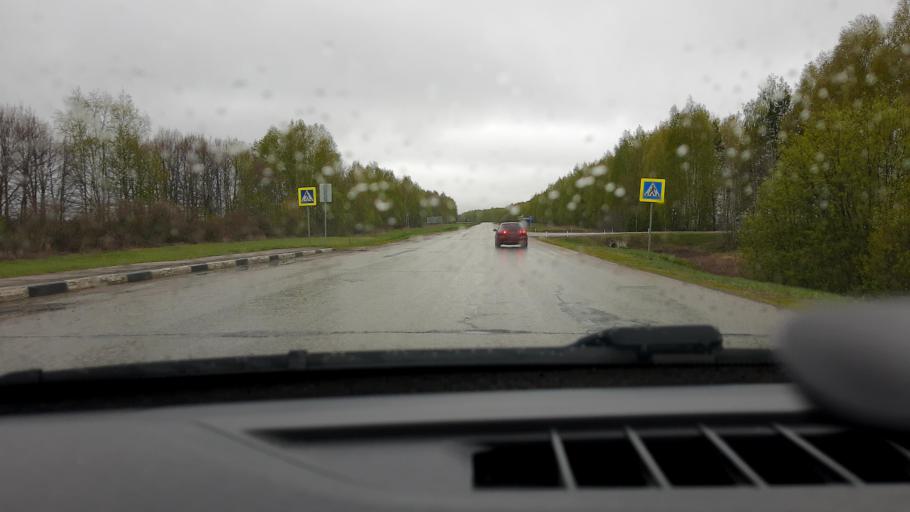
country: RU
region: Nizjnij Novgorod
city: Perevoz
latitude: 55.6144
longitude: 44.5081
